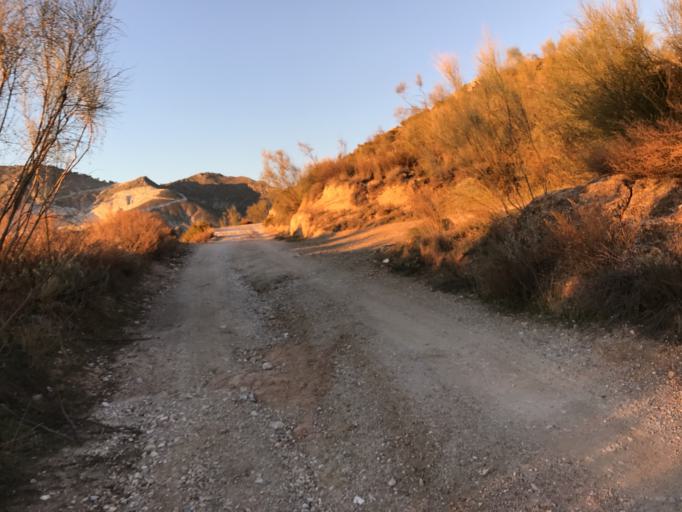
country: ES
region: Andalusia
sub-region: Provincia de Granada
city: Beas de Granada
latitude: 37.2258
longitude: -3.4720
